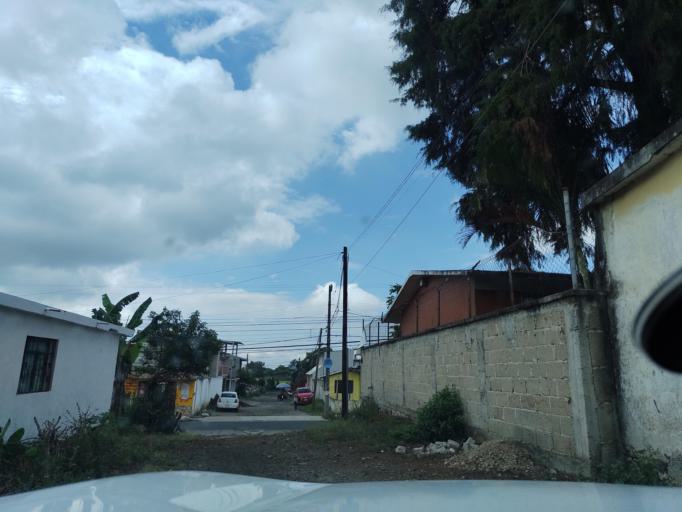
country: MX
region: Veracruz
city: Coatepec
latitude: 19.4823
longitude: -96.9343
